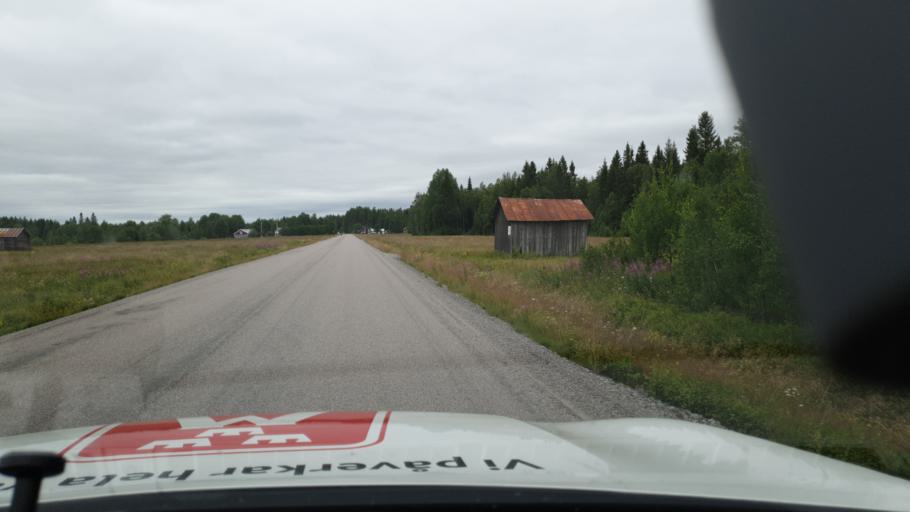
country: SE
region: Vaesterbotten
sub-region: Umea Kommun
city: Ersmark
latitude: 63.9130
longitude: 20.3098
